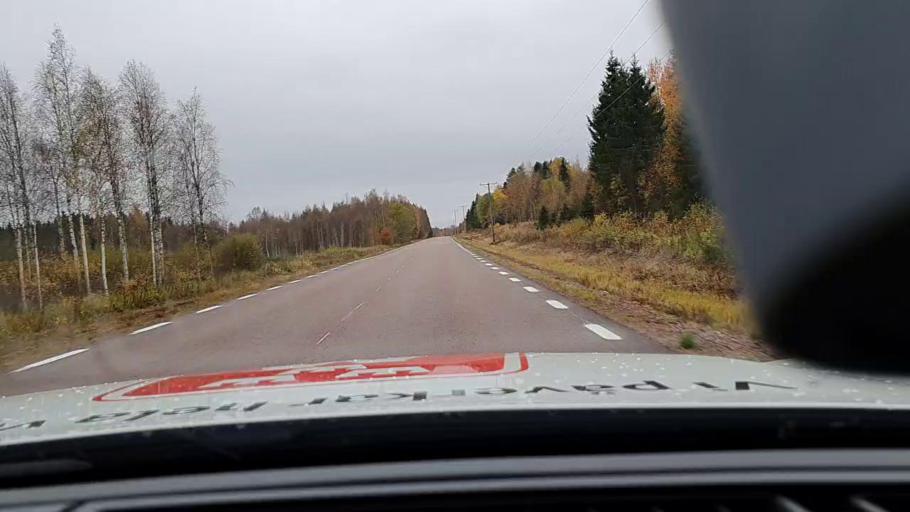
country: FI
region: Lapland
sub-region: Torniolaakso
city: Ylitornio
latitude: 66.1270
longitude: 23.9112
